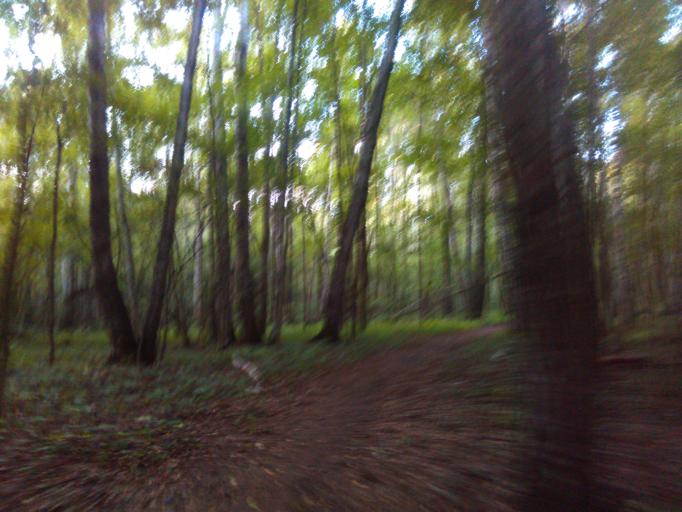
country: RU
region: Moskovskaya
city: Bogorodskoye
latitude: 55.8348
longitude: 37.6991
